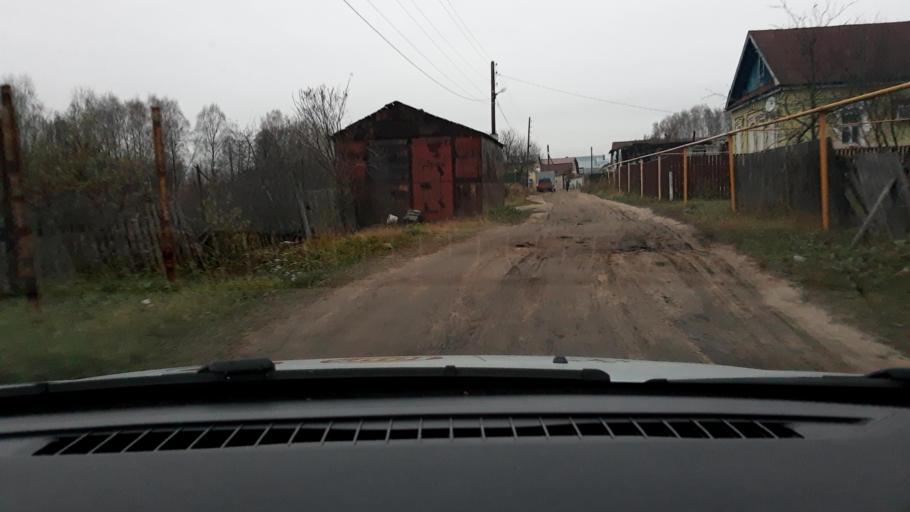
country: RU
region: Nizjnij Novgorod
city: Neklyudovo
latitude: 56.4237
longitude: 44.0135
